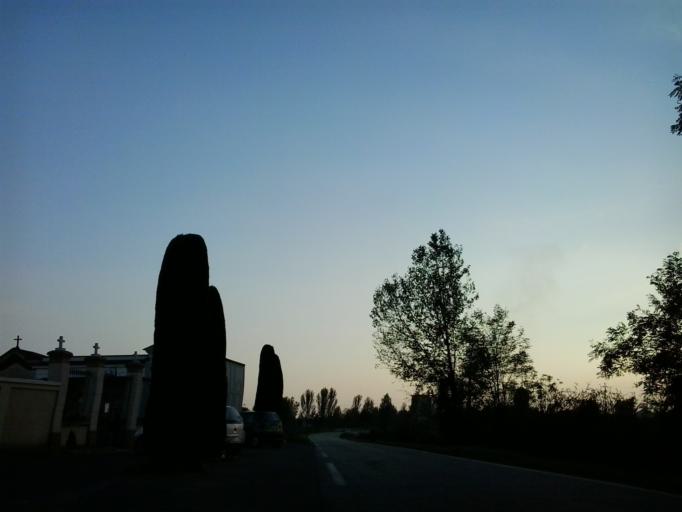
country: IT
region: Lombardy
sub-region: Provincia di Brescia
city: Offlaga
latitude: 45.4159
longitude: 10.1185
